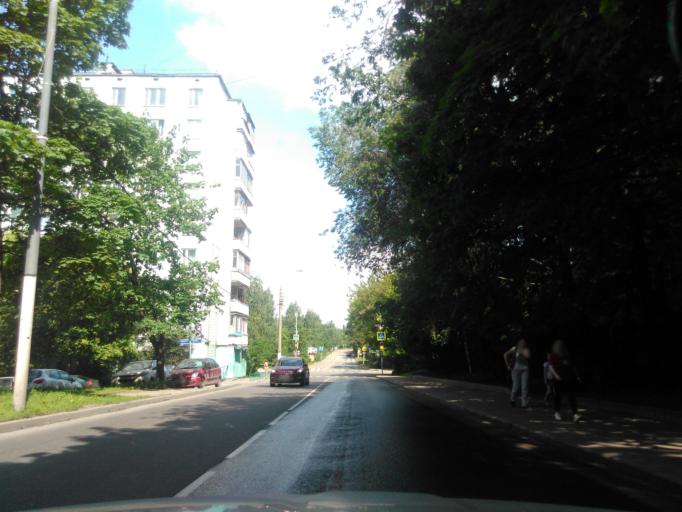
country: RU
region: Moscow
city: Vagonoremont
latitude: 55.8930
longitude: 37.5365
